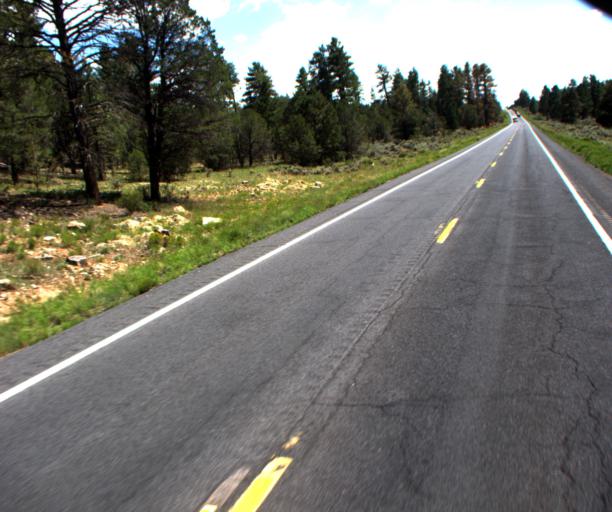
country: US
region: Arizona
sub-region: Coconino County
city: Grand Canyon Village
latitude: 35.8901
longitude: -112.1309
